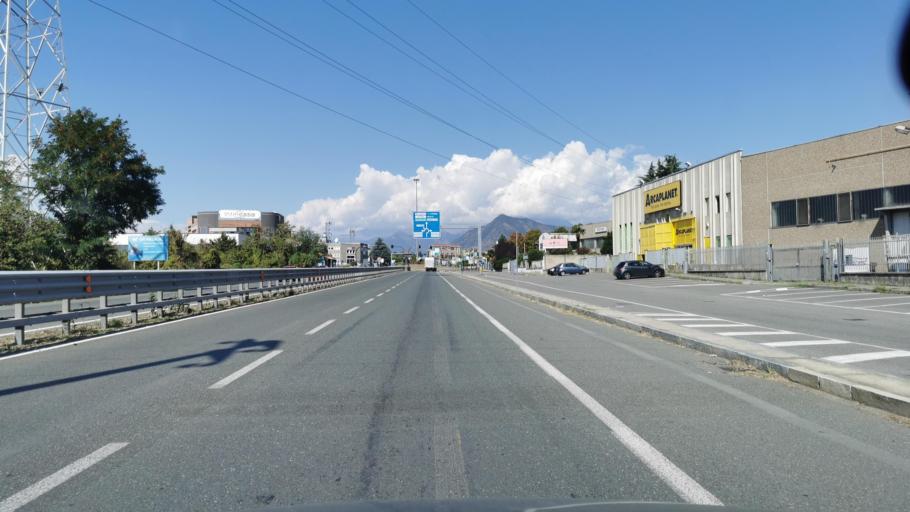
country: IT
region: Piedmont
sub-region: Provincia di Torino
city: Tetti Neirotti
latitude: 45.0604
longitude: 7.5522
